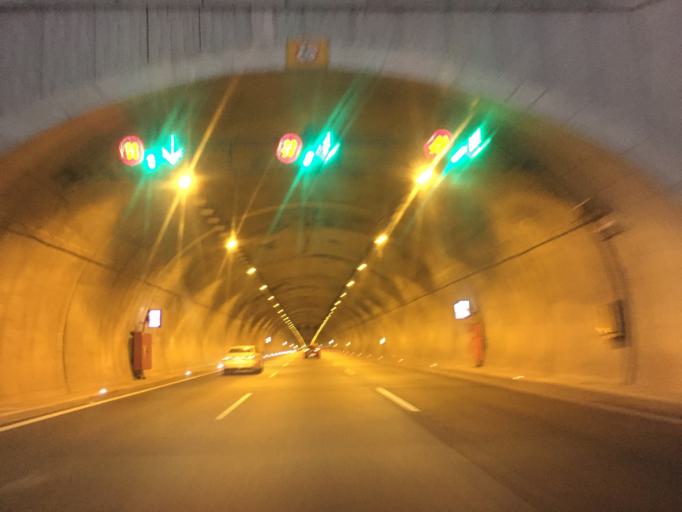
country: TR
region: Bursa
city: Demirtas
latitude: 40.3240
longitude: 29.0943
